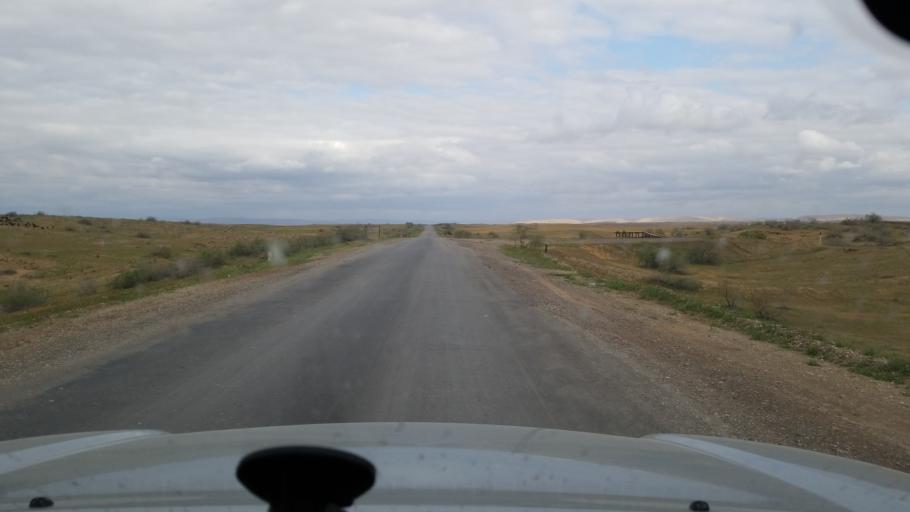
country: TM
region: Mary
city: Serhetabat
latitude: 35.9851
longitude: 62.6287
